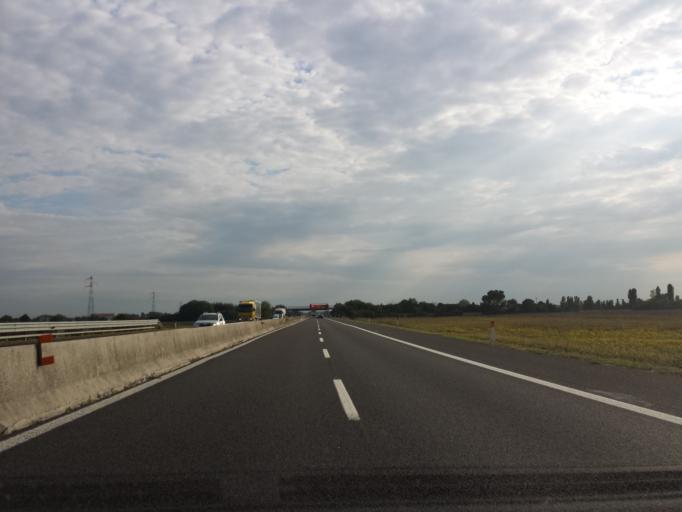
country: IT
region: Veneto
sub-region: Provincia di Padova
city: Stanghella
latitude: 45.1329
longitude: 11.7745
